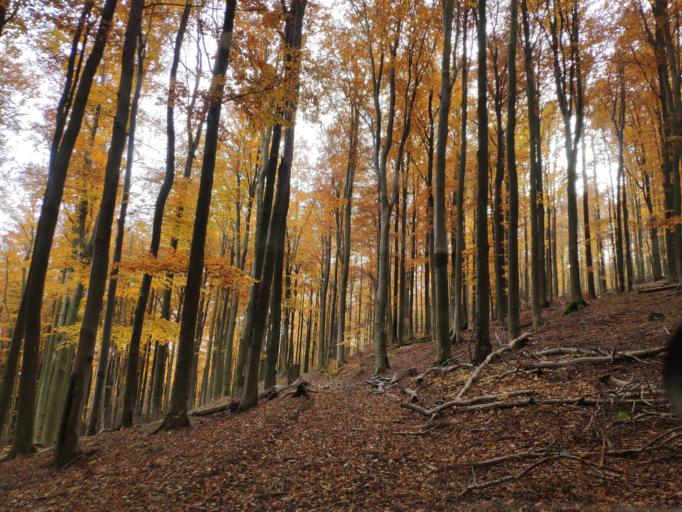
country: SK
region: Kosicky
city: Moldava nad Bodvou
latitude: 48.7363
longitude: 21.0144
